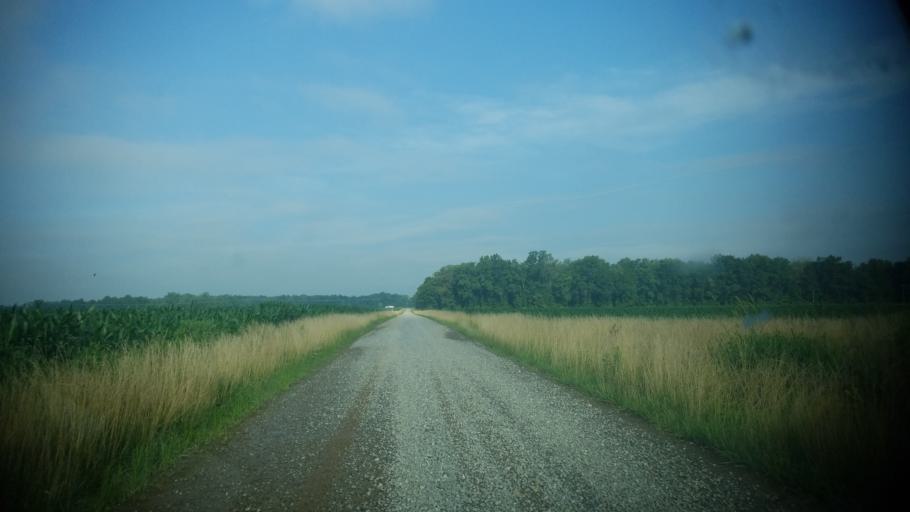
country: US
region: Illinois
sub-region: Clay County
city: Flora
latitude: 38.6019
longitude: -88.3550
